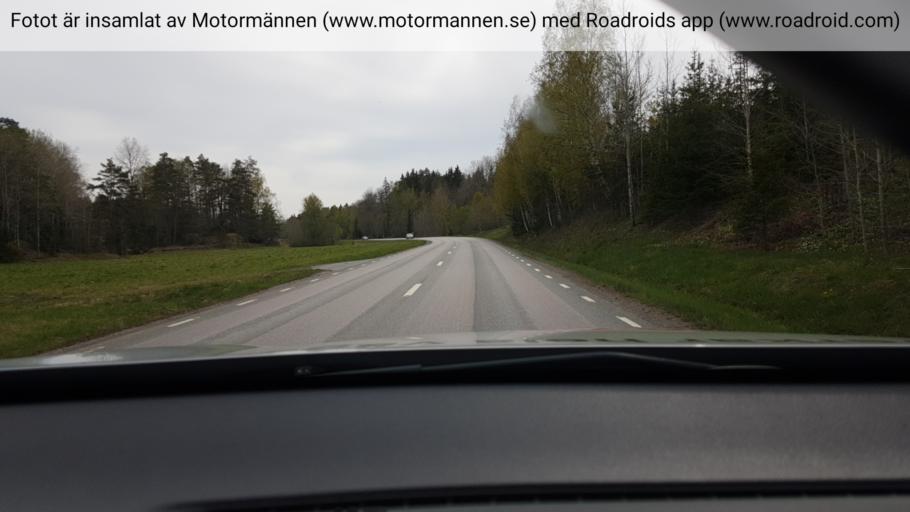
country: SE
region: Stockholm
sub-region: Norrtalje Kommun
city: Nykvarn
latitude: 59.9114
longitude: 18.0983
